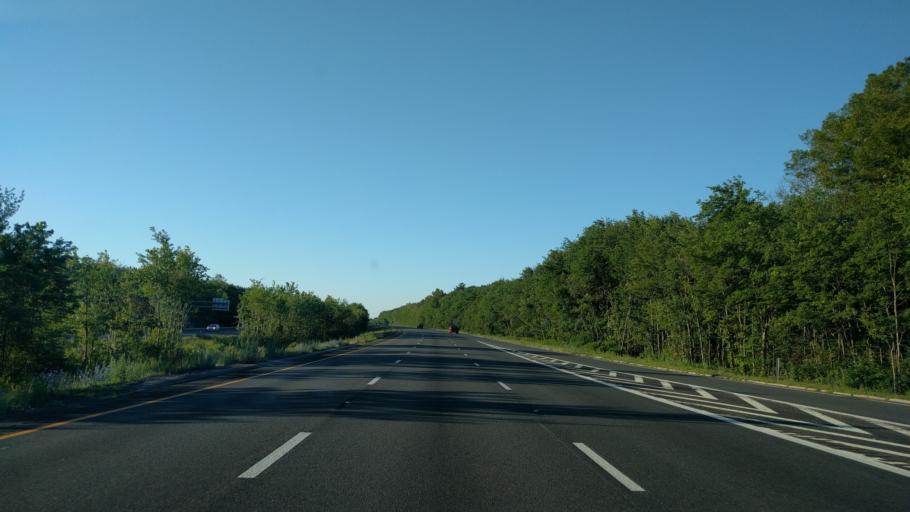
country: US
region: Massachusetts
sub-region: Worcester County
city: Milford
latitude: 42.1454
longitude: -71.4840
